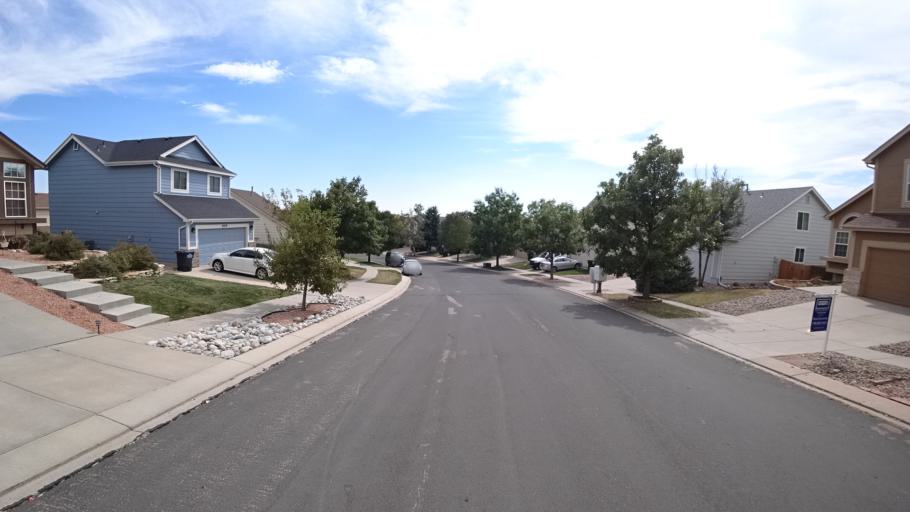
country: US
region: Colorado
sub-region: El Paso County
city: Cimarron Hills
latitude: 38.8989
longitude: -104.7185
